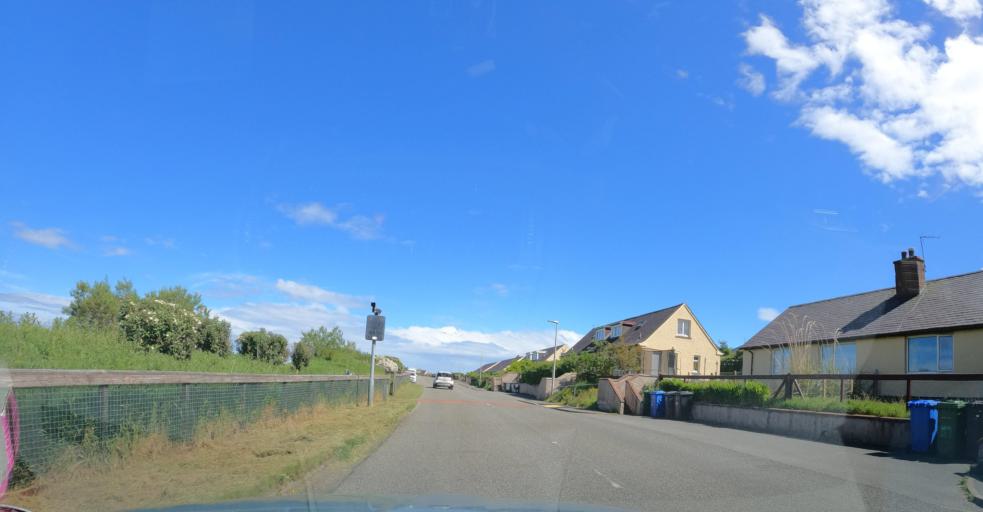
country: GB
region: Scotland
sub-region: Eilean Siar
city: Isle of Lewis
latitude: 58.2478
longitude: -6.3990
